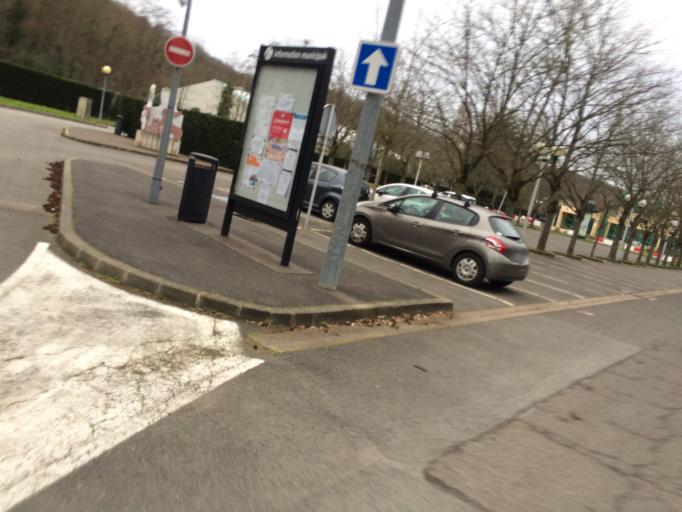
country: FR
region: Ile-de-France
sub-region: Departement de l'Essonne
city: Villebon-sur-Yvette
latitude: 48.6979
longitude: 2.2346
